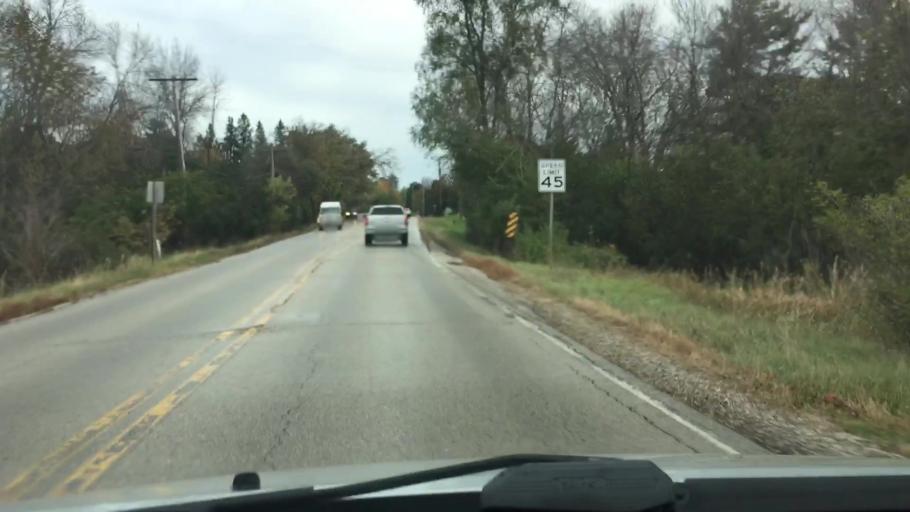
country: US
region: Wisconsin
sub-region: Waukesha County
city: Pewaukee
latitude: 43.0546
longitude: -88.2846
